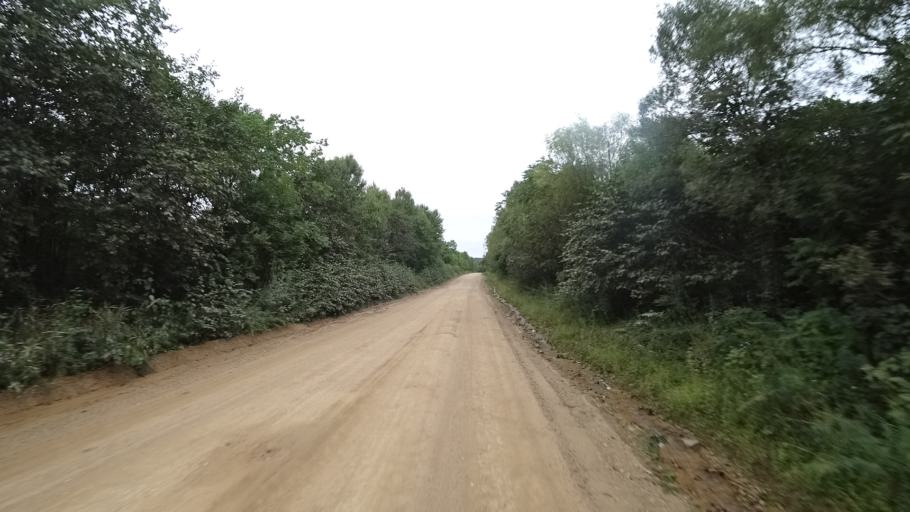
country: RU
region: Primorskiy
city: Rettikhovka
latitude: 44.1780
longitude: 132.8029
